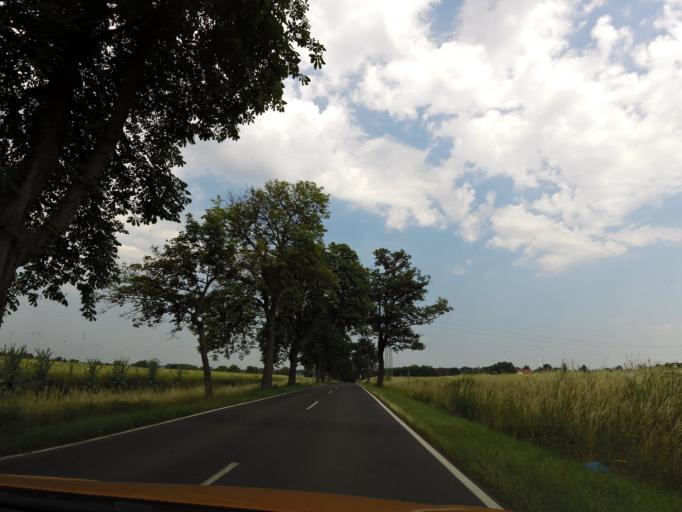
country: DE
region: Brandenburg
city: Nauen
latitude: 52.5670
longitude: 12.8696
